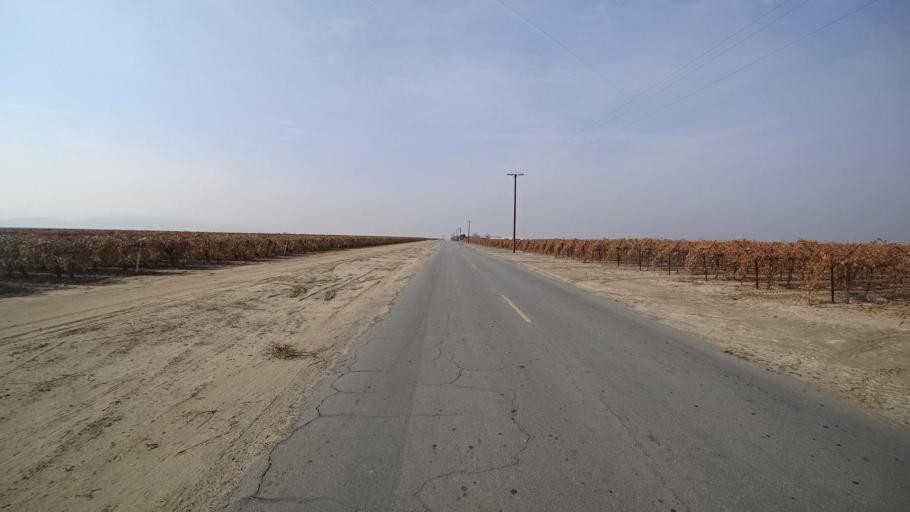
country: US
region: California
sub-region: Kern County
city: Weedpatch
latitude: 35.0744
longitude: -118.9231
